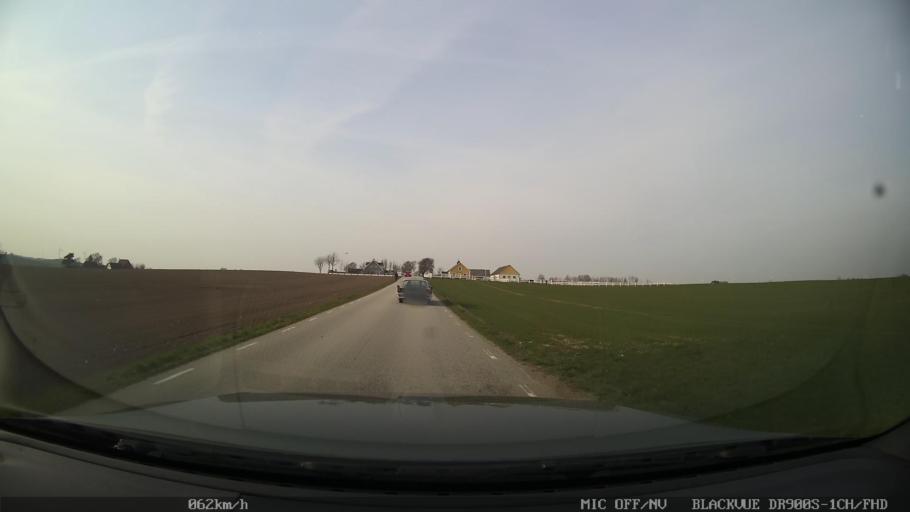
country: SE
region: Skane
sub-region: Ystads Kommun
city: Ystad
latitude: 55.4558
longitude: 13.8294
